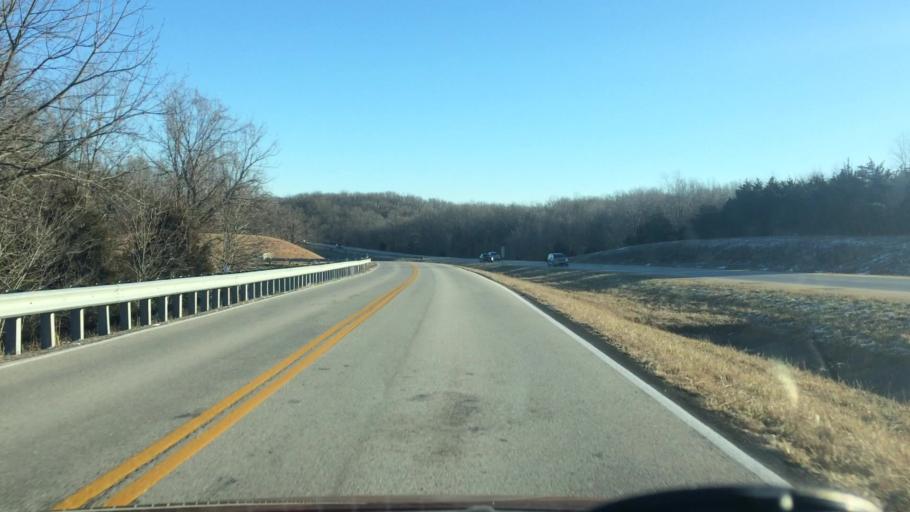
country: US
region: Missouri
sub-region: Greene County
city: Strafford
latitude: 37.2743
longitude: -93.0514
